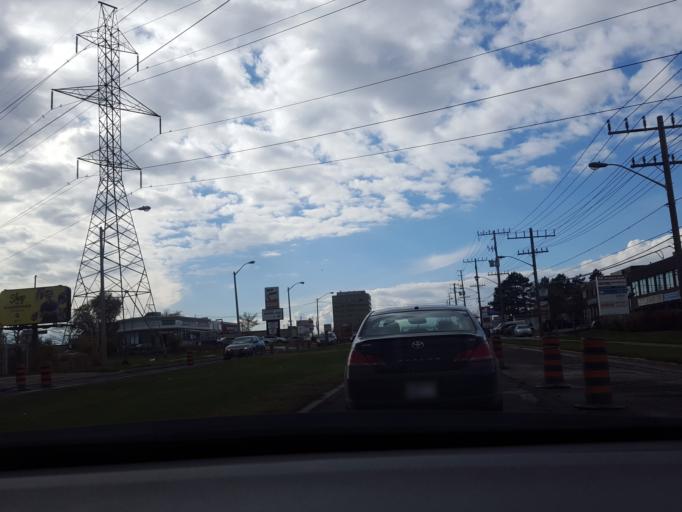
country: CA
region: Ontario
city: Etobicoke
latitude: 43.7126
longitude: -79.5626
